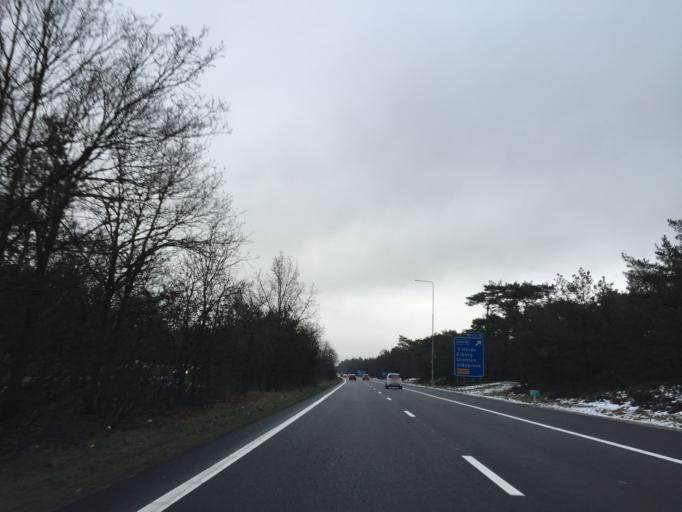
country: NL
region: Gelderland
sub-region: Gemeente Oldebroek
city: Oldebroek
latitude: 52.4016
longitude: 5.8753
